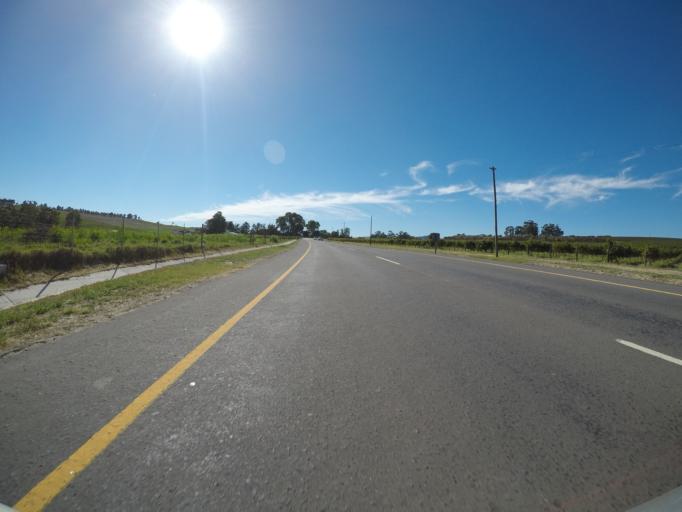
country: ZA
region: Western Cape
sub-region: Cape Winelands District Municipality
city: Stellenbosch
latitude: -33.9895
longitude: 18.7586
